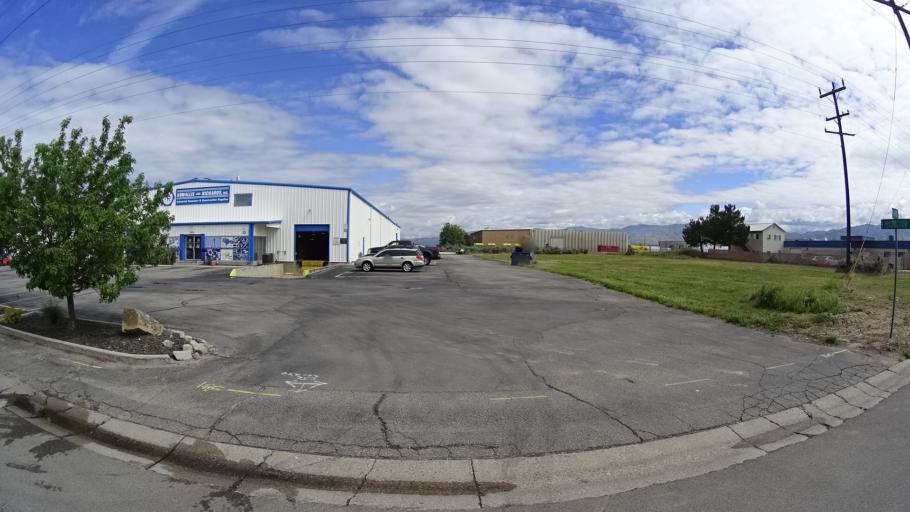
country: US
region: Idaho
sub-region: Ada County
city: Boise
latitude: 43.5604
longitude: -116.1934
